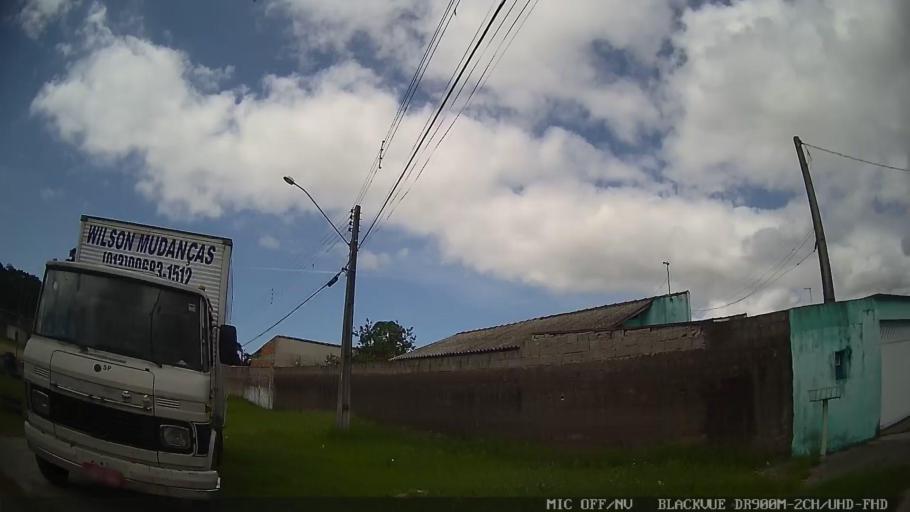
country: BR
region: Sao Paulo
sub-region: Peruibe
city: Peruibe
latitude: -24.2919
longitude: -47.0174
